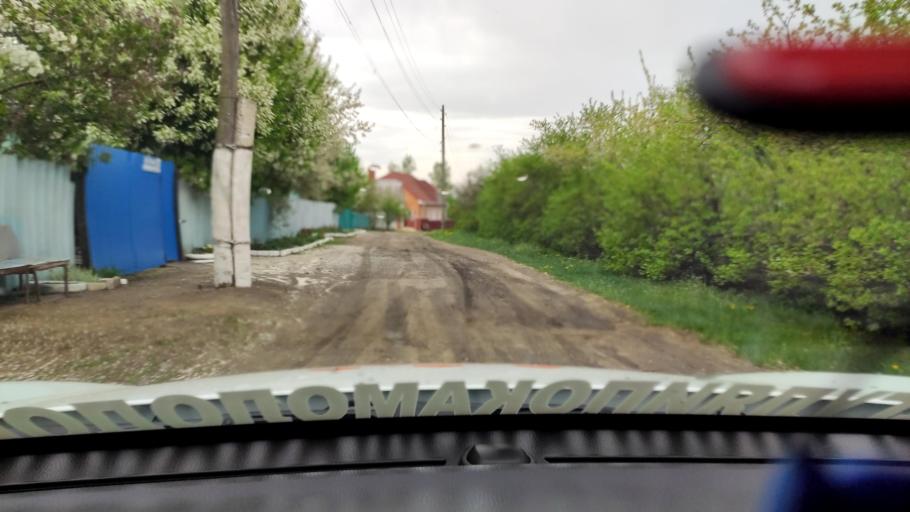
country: RU
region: Voronezj
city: Uryv-Pokrovka
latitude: 51.1213
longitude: 39.1720
